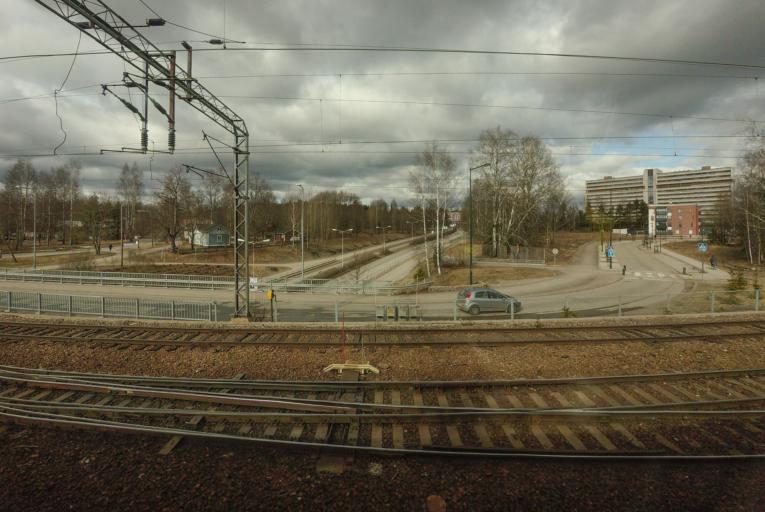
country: FI
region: Kymenlaakso
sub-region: Kouvola
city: Kouvola
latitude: 60.8648
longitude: 26.6934
